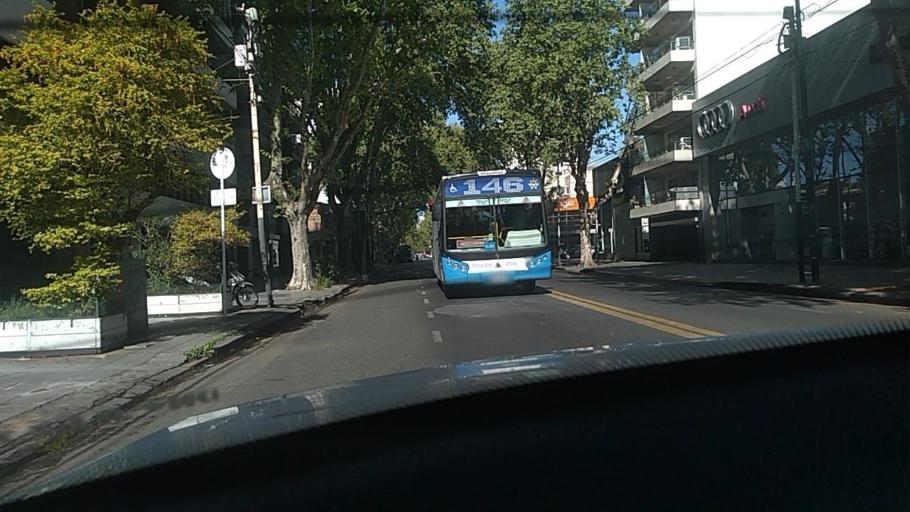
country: AR
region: Buenos Aires F.D.
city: Villa Santa Rita
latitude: -34.5987
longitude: -58.5002
